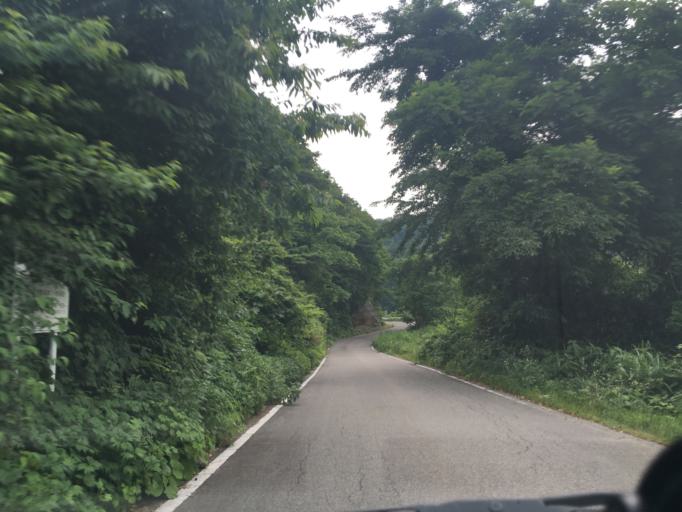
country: JP
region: Fukushima
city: Kitakata
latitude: 37.4852
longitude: 139.7784
